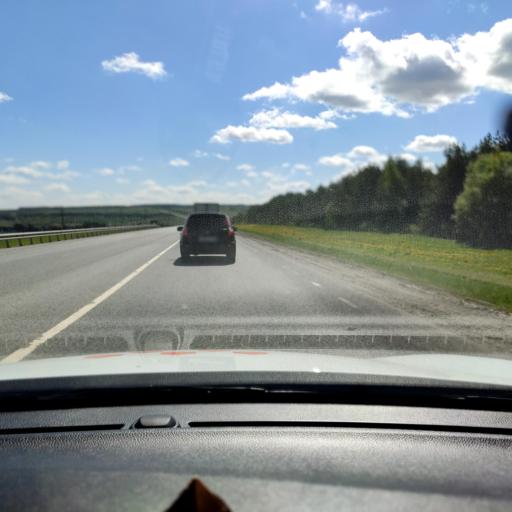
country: RU
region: Tatarstan
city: Sviyazhsk
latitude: 55.7269
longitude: 48.8162
